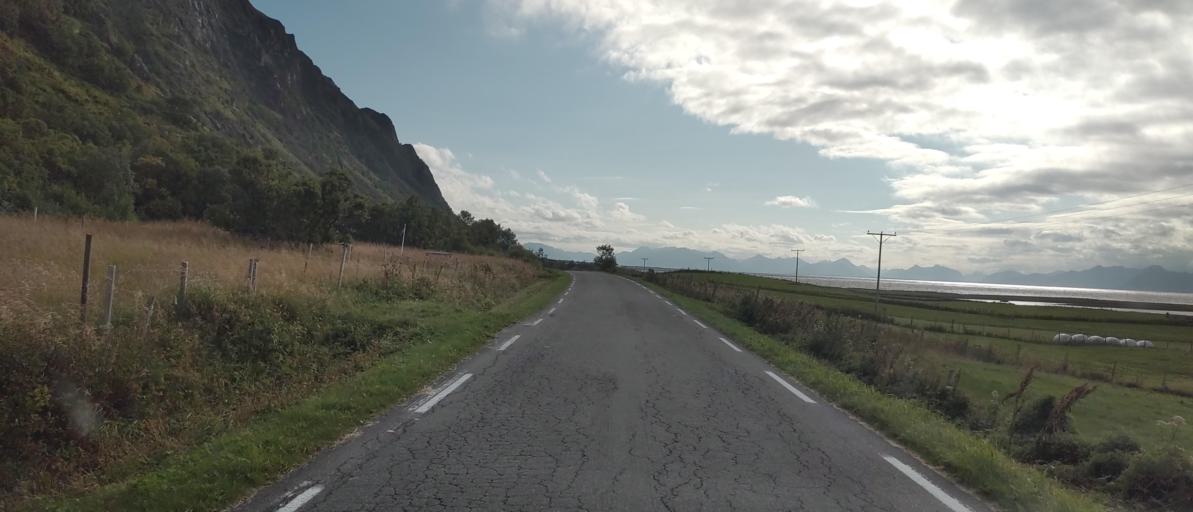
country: NO
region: Nordland
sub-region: Sortland
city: Sortland
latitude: 69.0683
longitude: 15.5418
